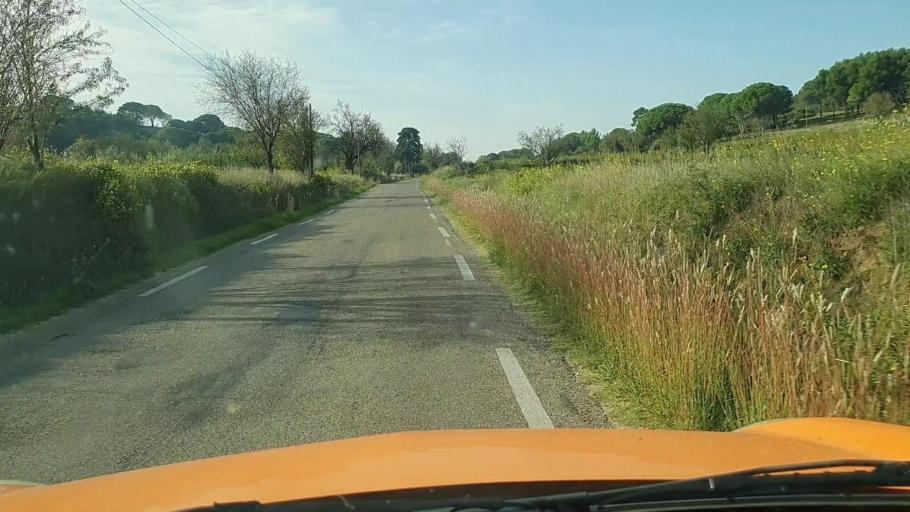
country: FR
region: Languedoc-Roussillon
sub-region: Departement du Gard
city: Generac
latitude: 43.7236
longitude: 4.3429
